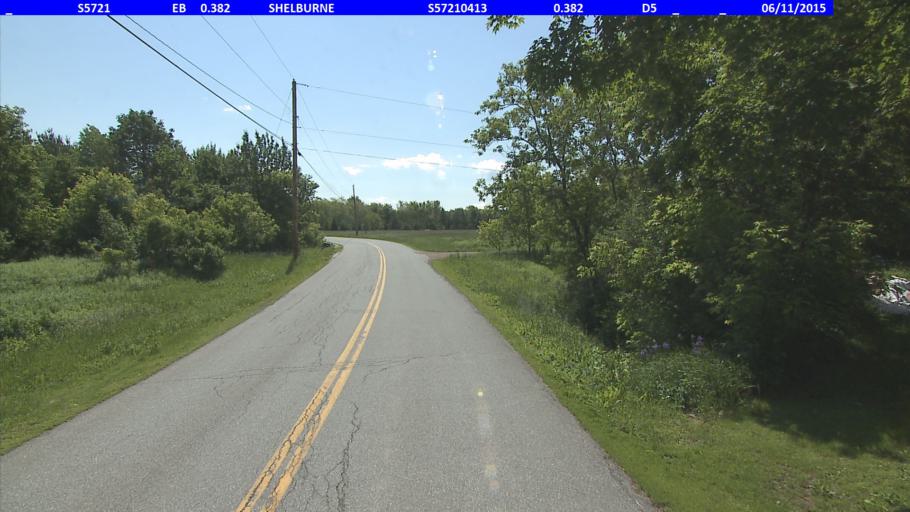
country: US
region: Vermont
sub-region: Chittenden County
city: Hinesburg
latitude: 44.3656
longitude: -73.2130
